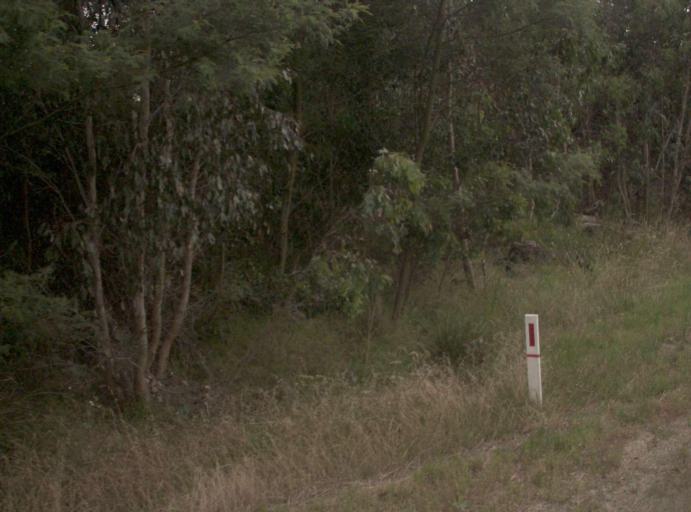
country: AU
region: Victoria
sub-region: Latrobe
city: Traralgon
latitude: -38.5551
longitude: 146.8142
